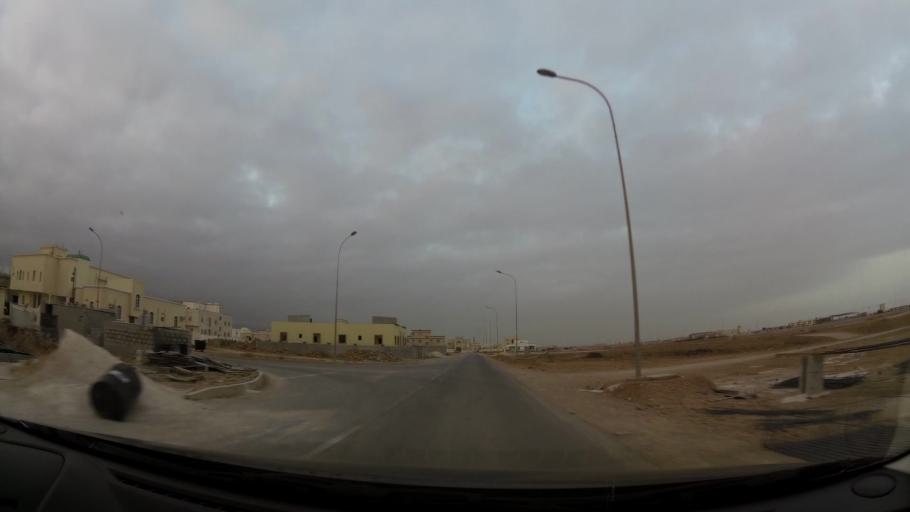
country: OM
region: Zufar
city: Salalah
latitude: 17.0308
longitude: 54.0246
